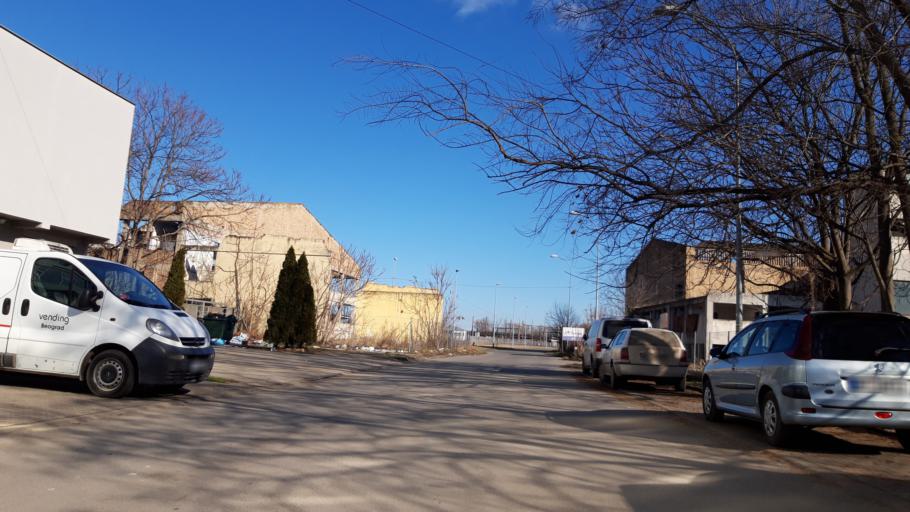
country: RS
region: Autonomna Pokrajina Vojvodina
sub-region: Juznobacki Okrug
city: Novi Sad
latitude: 45.2718
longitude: 19.8421
